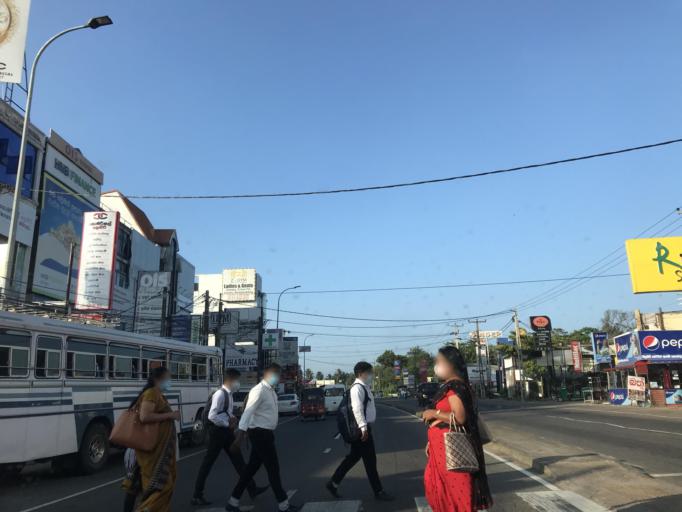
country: LK
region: Western
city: Ja Ela
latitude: 7.0827
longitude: 79.8911
